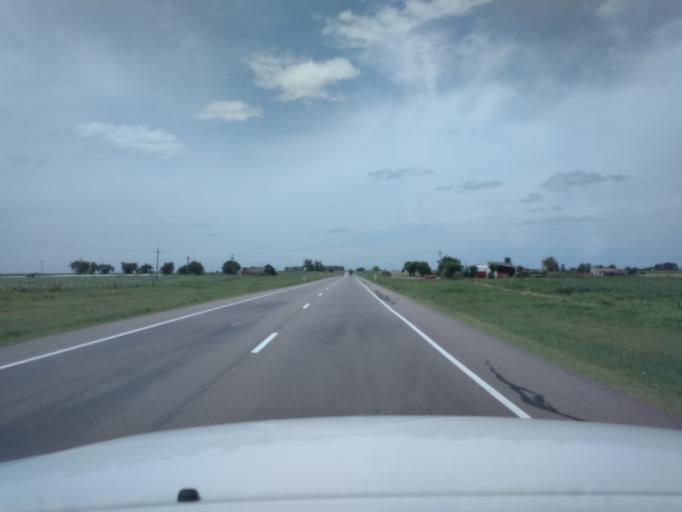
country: UY
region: Florida
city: Cardal
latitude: -34.3161
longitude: -56.2413
